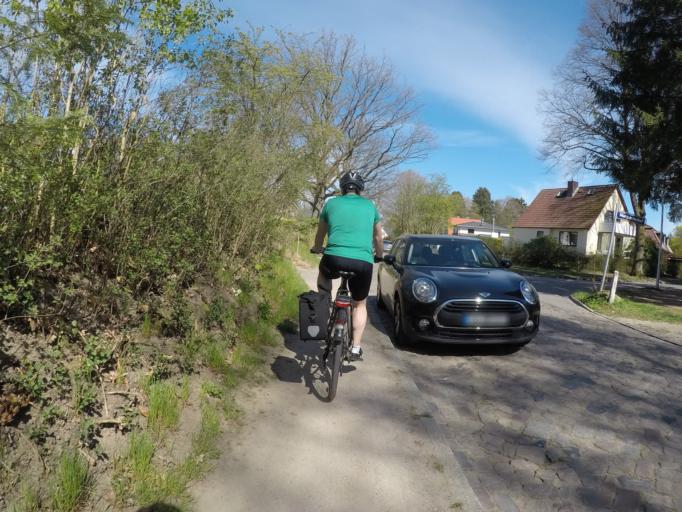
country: DE
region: Hamburg
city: Lemsahl-Mellingstedt
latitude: 53.6778
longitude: 10.1047
